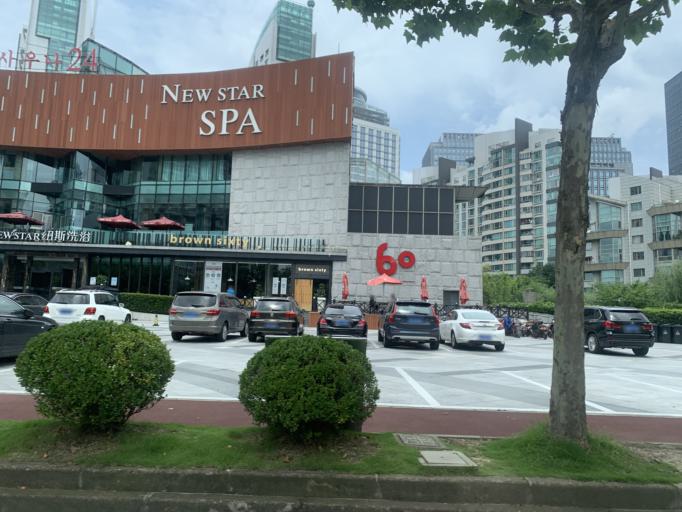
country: CN
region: Shanghai Shi
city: Huamu
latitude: 31.2125
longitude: 121.5335
